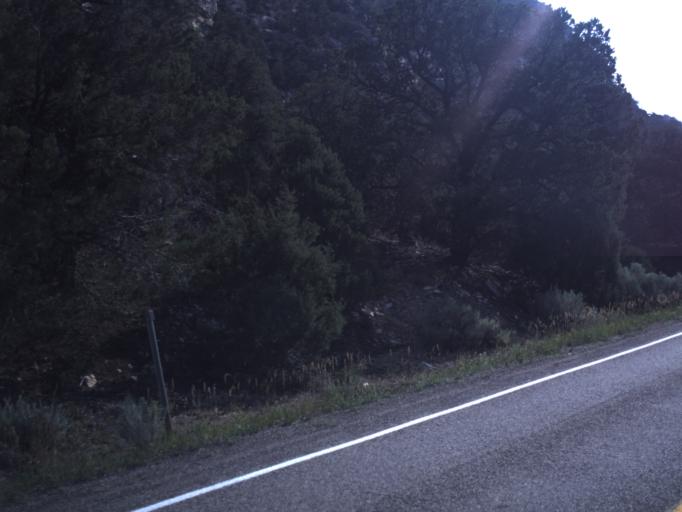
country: US
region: Utah
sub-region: Daggett County
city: Manila
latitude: 40.9527
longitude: -109.4647
